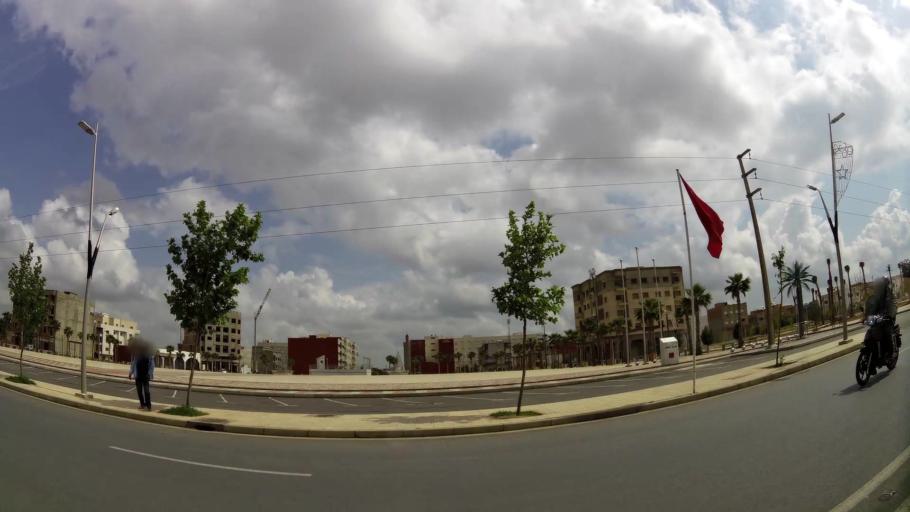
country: MA
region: Rabat-Sale-Zemmour-Zaer
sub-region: Khemisset
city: Tiflet
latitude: 33.8948
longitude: -6.3388
